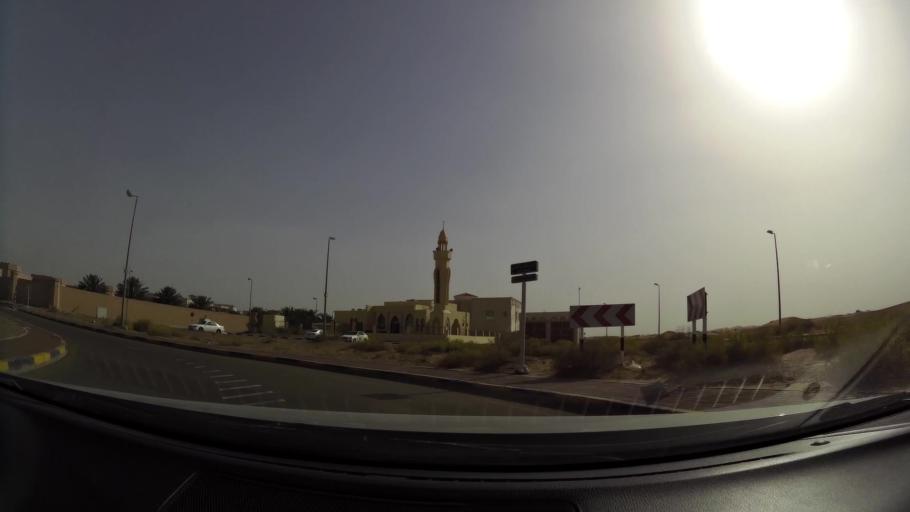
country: AE
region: Abu Dhabi
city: Al Ain
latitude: 24.2268
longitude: 55.6544
